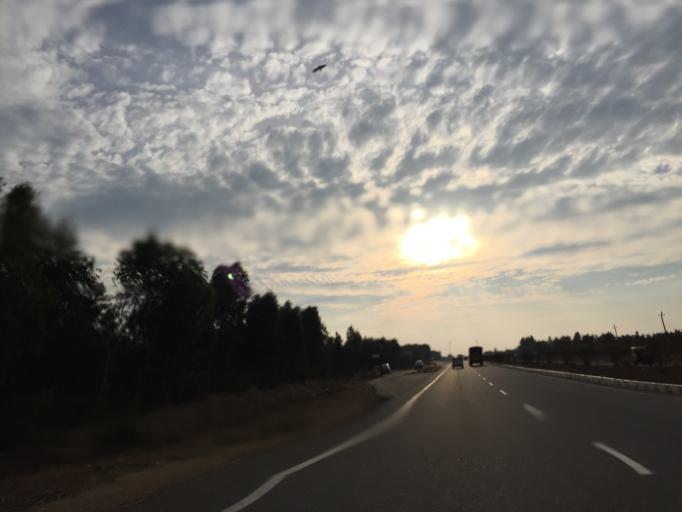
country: IN
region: Karnataka
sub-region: Kolar
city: Kolar
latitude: 13.1437
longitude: 78.2378
